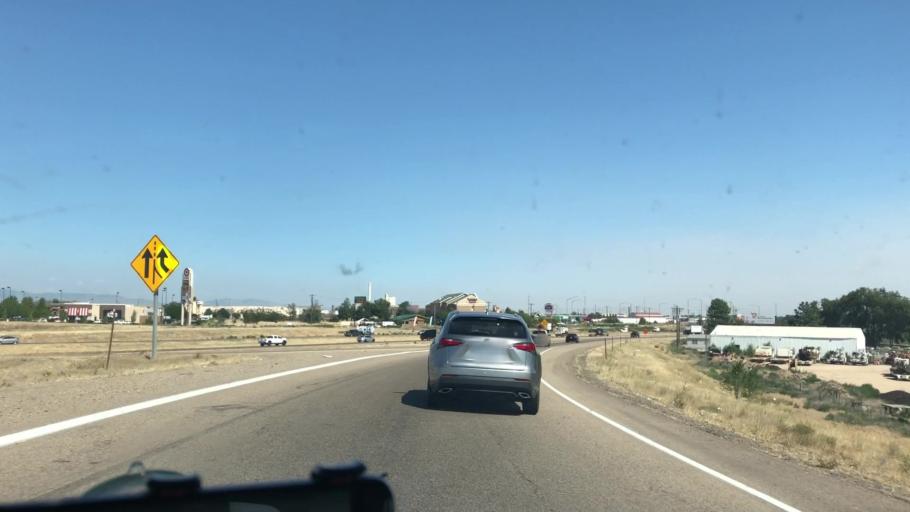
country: US
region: Idaho
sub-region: Canyon County
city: Nampa
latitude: 43.6085
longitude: -116.5969
